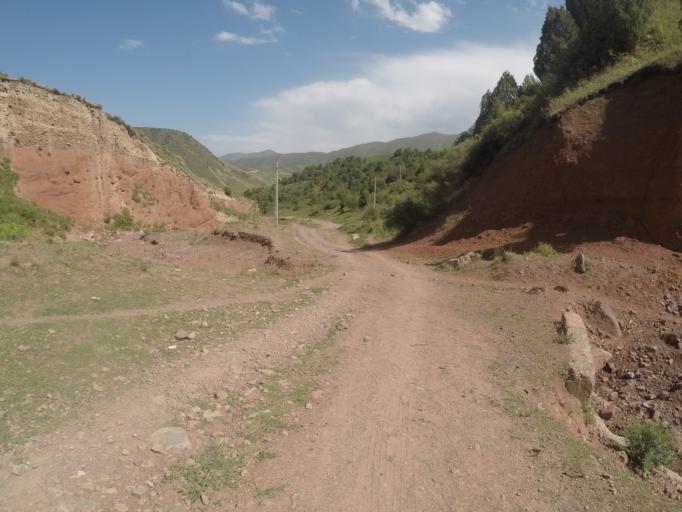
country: KG
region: Chuy
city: Bishkek
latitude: 42.6430
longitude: 74.6049
